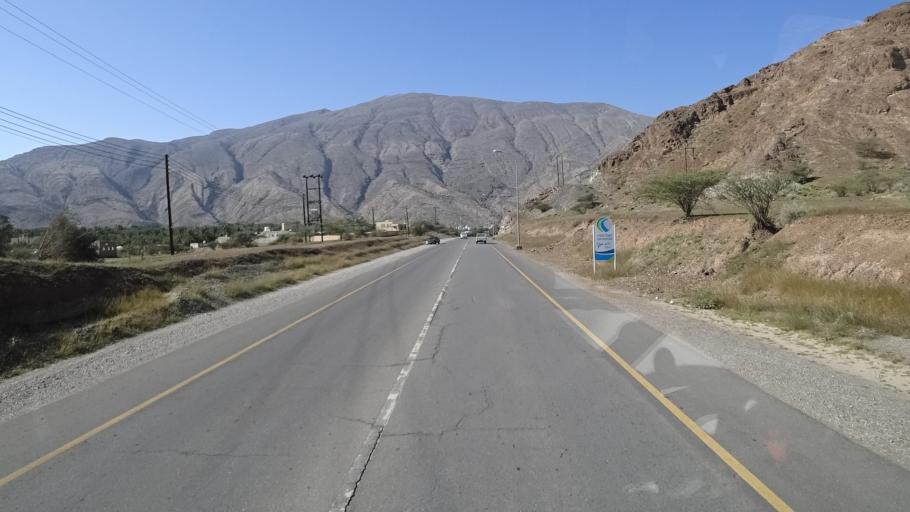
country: OM
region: Al Batinah
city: Bayt al `Awabi
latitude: 23.3146
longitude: 57.5293
